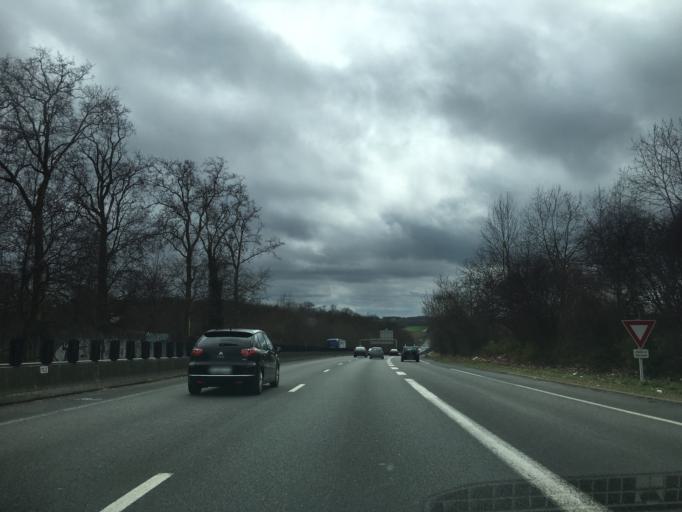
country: FR
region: Ile-de-France
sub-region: Departement de Seine-et-Marne
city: Brie-Comte-Robert
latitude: 48.6757
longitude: 2.6103
